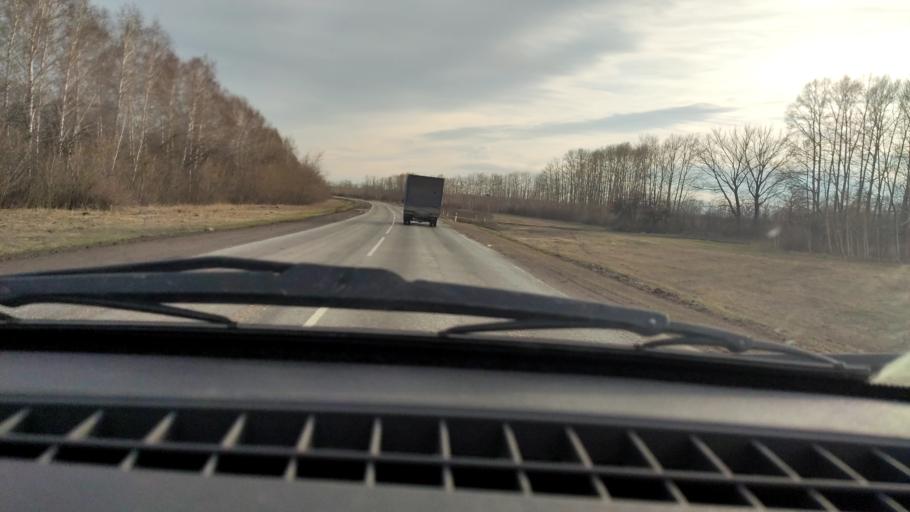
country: RU
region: Bashkortostan
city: Davlekanovo
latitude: 54.3524
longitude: 55.1807
